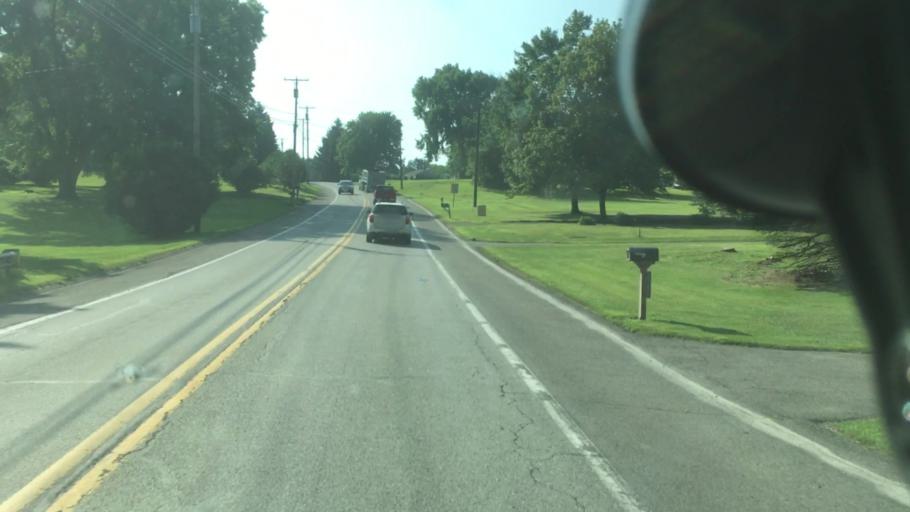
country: US
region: Pennsylvania
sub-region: Lawrence County
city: Oakwood
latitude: 41.0202
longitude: -80.4172
